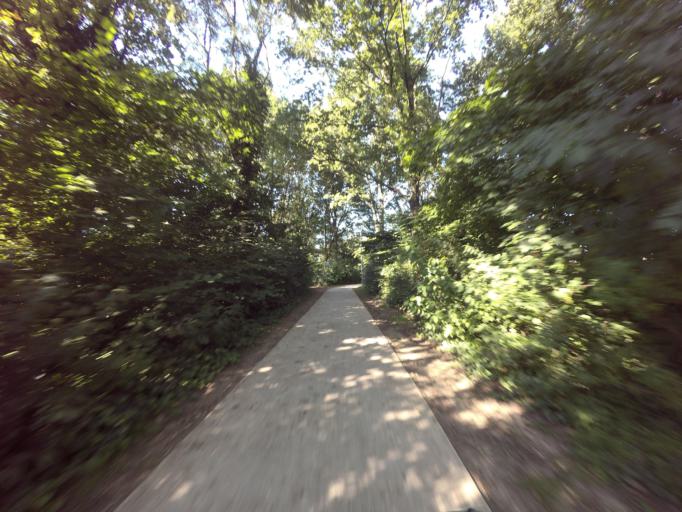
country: NL
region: Overijssel
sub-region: Gemeente Hardenberg
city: Hardenberg
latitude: 52.5654
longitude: 6.6097
